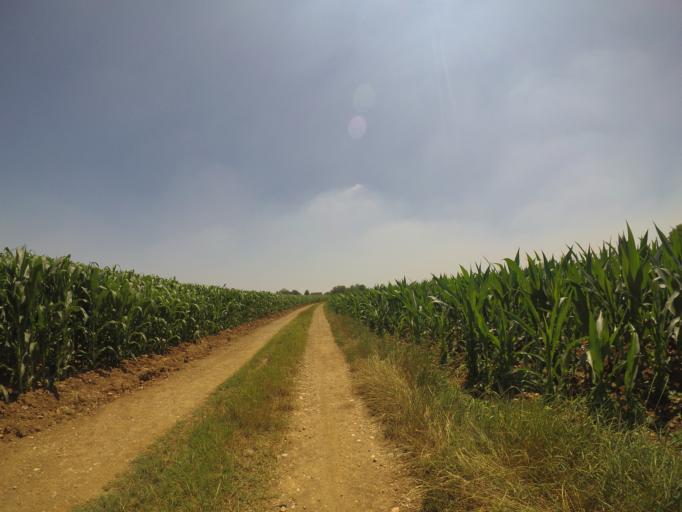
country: IT
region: Friuli Venezia Giulia
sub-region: Provincia di Udine
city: Bertiolo
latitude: 45.9477
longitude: 13.0280
